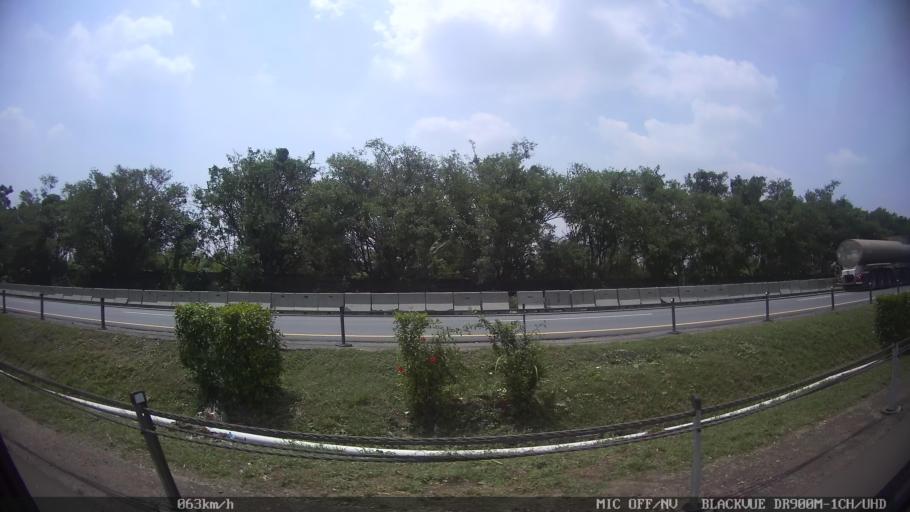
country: ID
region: West Java
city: Kresek
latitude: -6.1436
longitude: 106.2795
